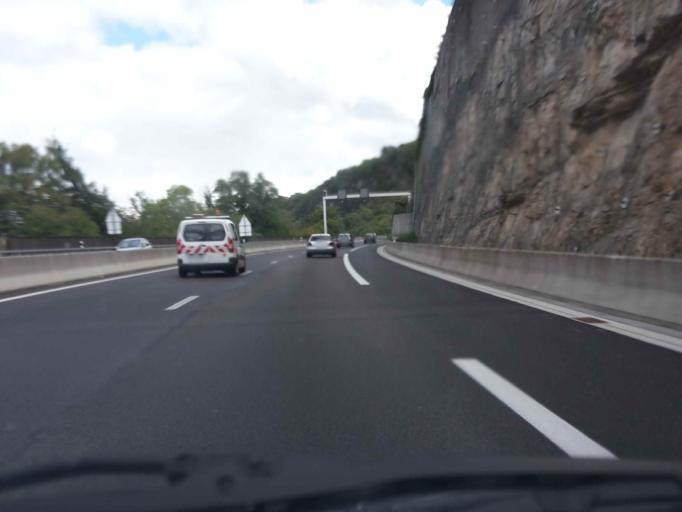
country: FR
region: Franche-Comte
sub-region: Departement du Doubs
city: Beure
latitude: 47.2159
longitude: 6.0133
